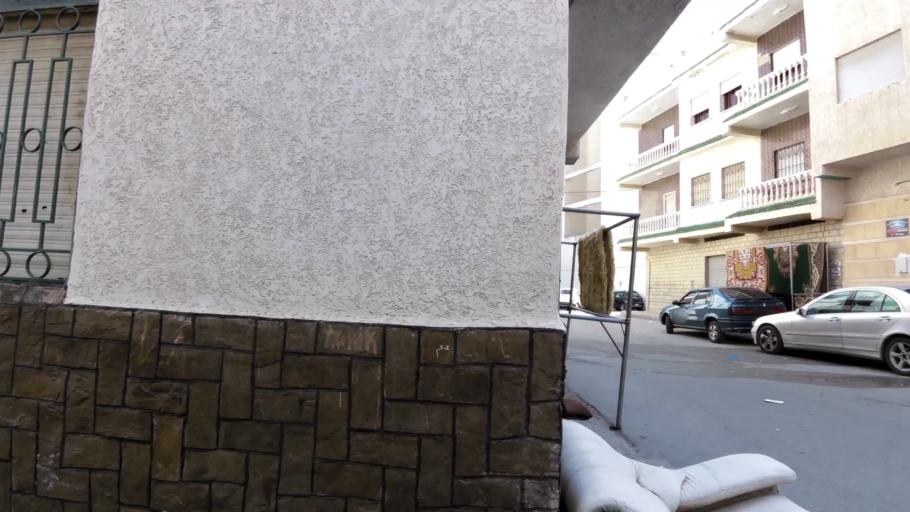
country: MA
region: Tanger-Tetouan
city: Tetouan
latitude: 35.5832
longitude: -5.3523
